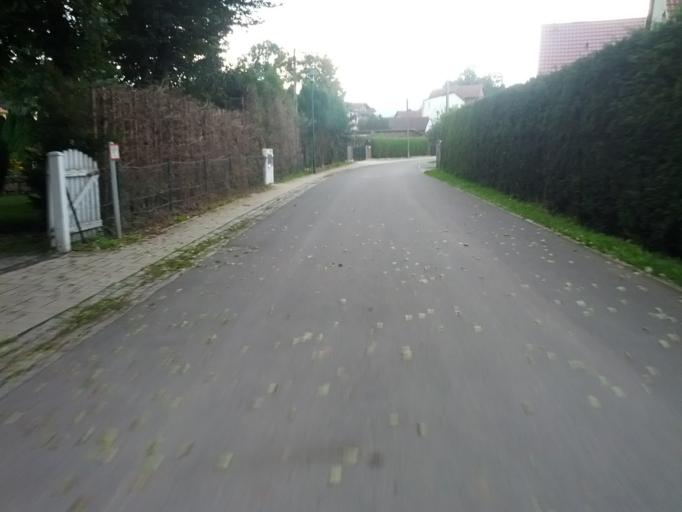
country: DE
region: Thuringia
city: Thal
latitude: 50.9446
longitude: 10.3917
